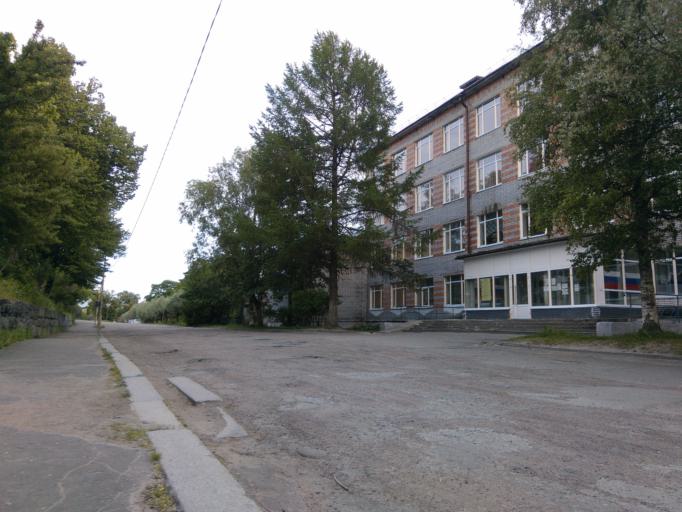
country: RU
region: Republic of Karelia
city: Sortavala
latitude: 61.7050
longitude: 30.6848
